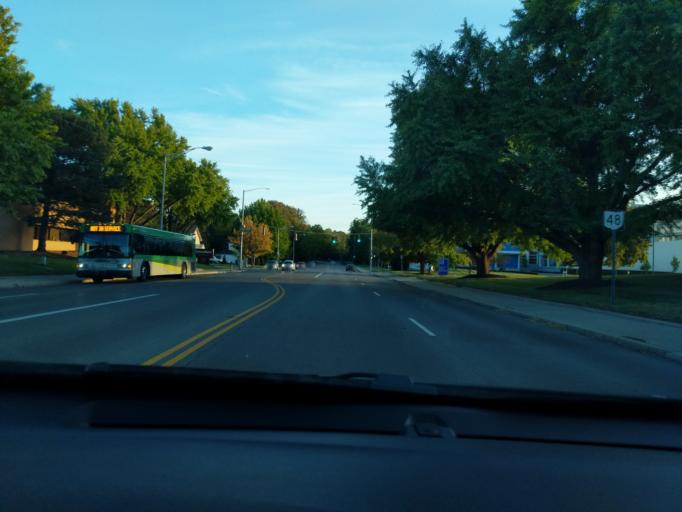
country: US
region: Ohio
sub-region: Montgomery County
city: Oakwood
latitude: 39.7384
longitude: -84.1861
